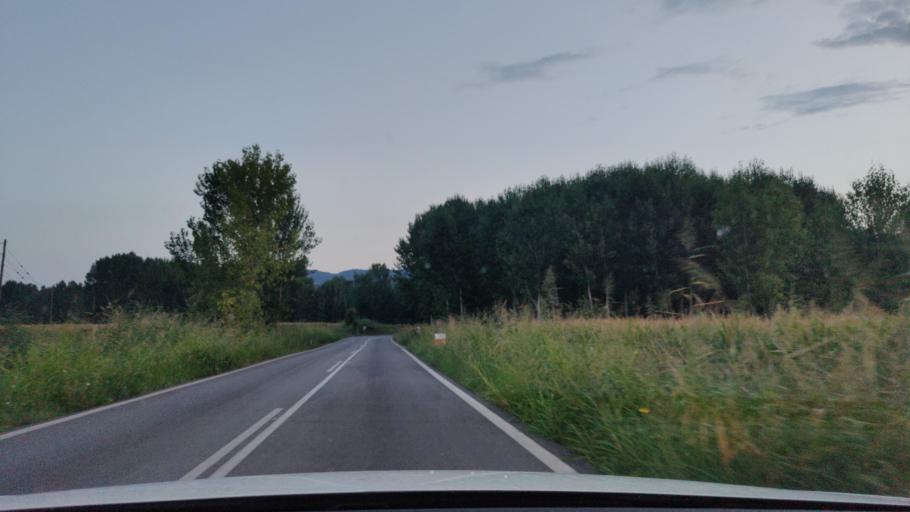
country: GR
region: Central Macedonia
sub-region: Nomos Serron
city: Chrysochorafa
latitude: 41.1439
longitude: 23.2307
